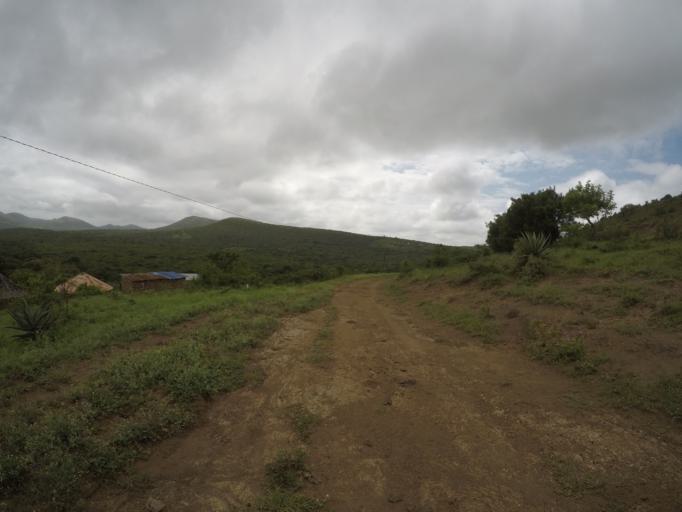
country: ZA
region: KwaZulu-Natal
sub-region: uThungulu District Municipality
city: Empangeni
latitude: -28.6272
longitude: 31.8774
